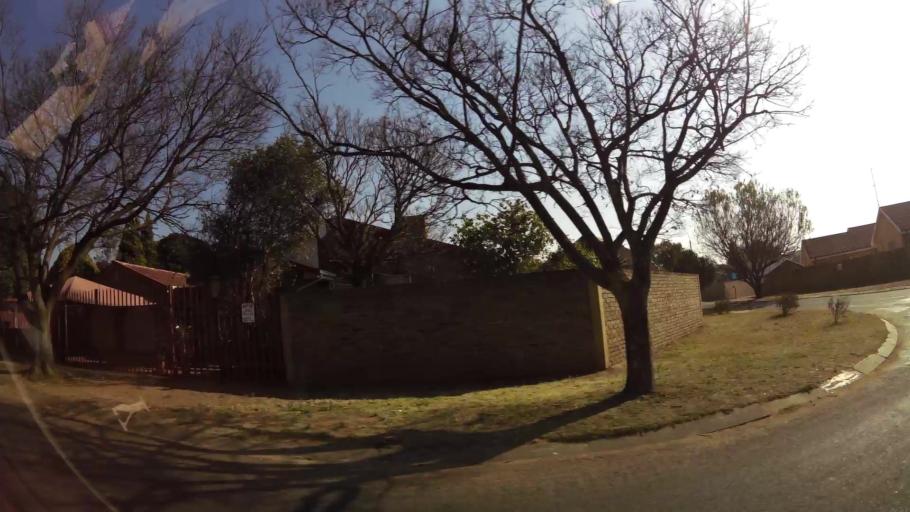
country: ZA
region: Gauteng
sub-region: West Rand District Municipality
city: Randfontein
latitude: -26.1849
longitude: 27.6808
